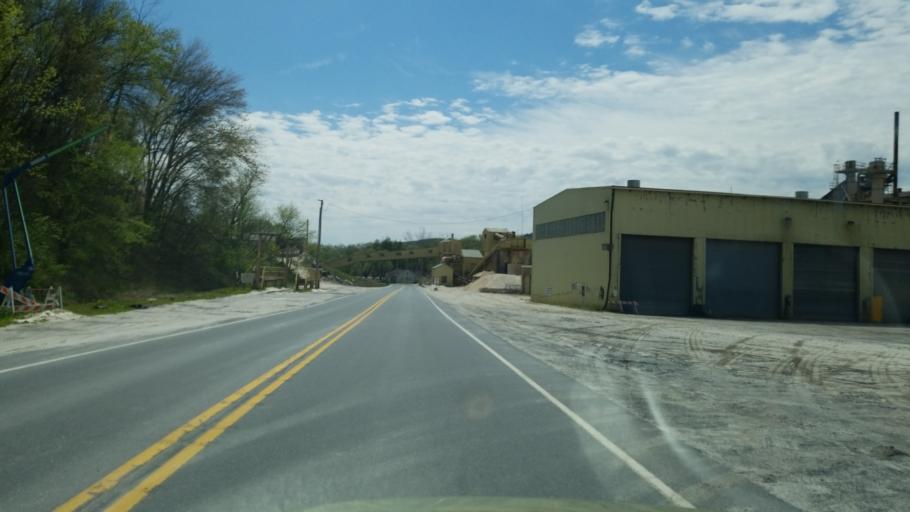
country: US
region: Pennsylvania
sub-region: Huntingdon County
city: Mount Union
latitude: 40.4090
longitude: -77.9347
